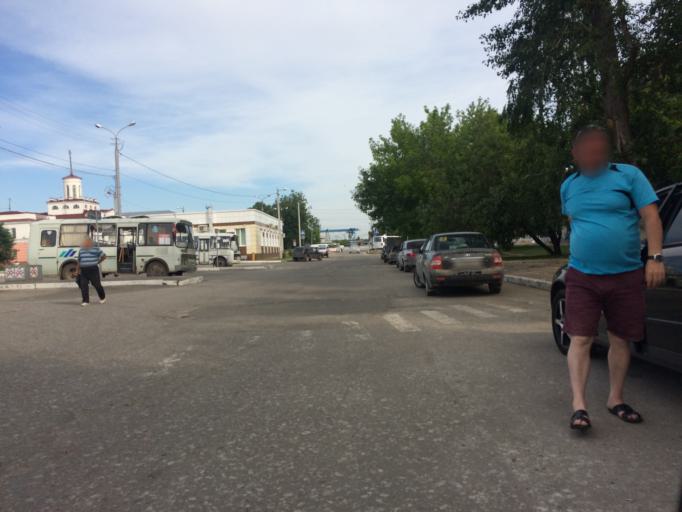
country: RU
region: Mariy-El
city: Yoshkar-Ola
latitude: 56.6212
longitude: 47.8824
